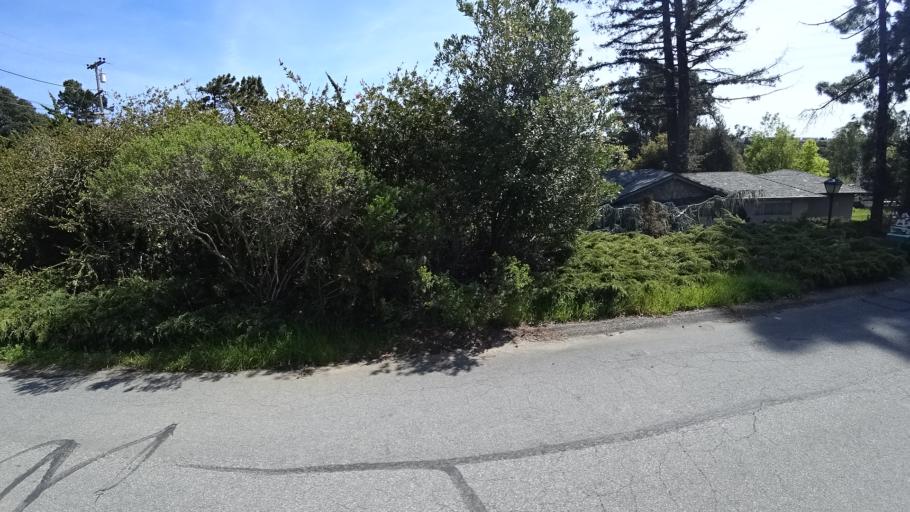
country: US
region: California
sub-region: Alameda County
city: Fairview
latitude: 37.6590
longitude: -122.0280
